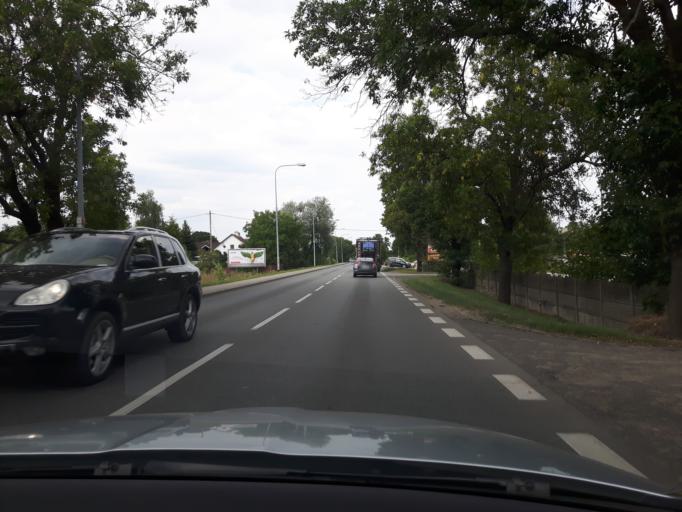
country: PL
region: Masovian Voivodeship
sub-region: Powiat legionowski
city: Stanislawow Pierwszy
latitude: 52.3460
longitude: 21.0287
